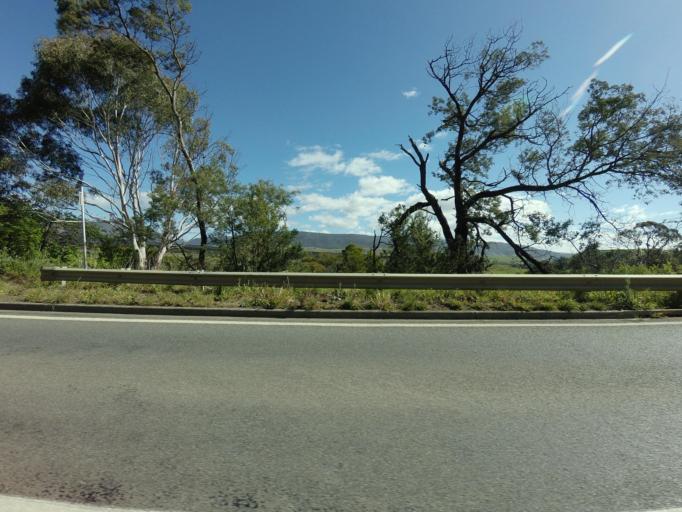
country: AU
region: Tasmania
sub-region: Derwent Valley
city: New Norfolk
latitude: -42.7346
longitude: 146.9749
